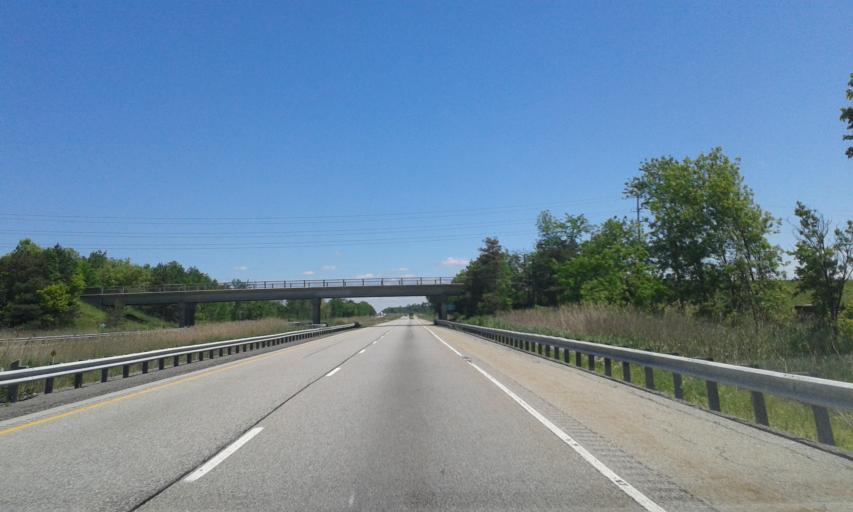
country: US
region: New York
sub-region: St. Lawrence County
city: Norfolk
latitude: 44.8913
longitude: -75.2608
